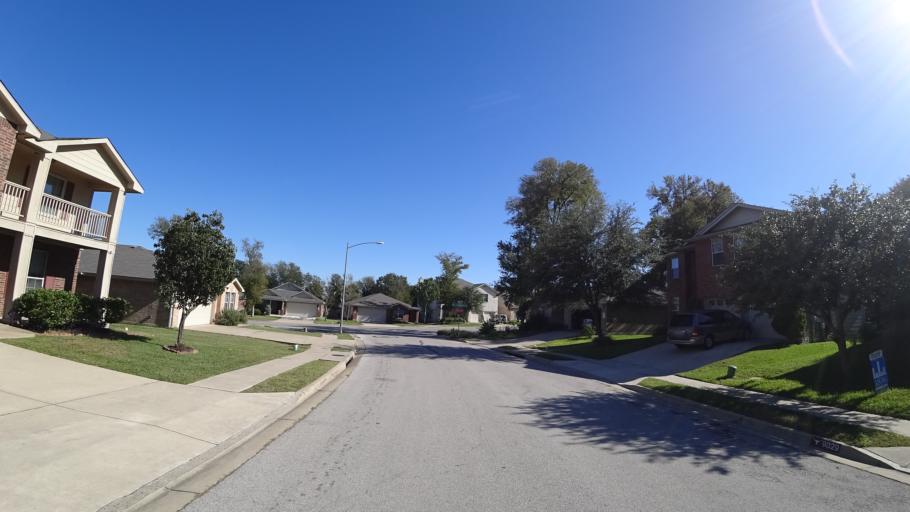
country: US
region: Texas
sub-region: Travis County
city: Hornsby Bend
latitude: 30.2766
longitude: -97.6319
